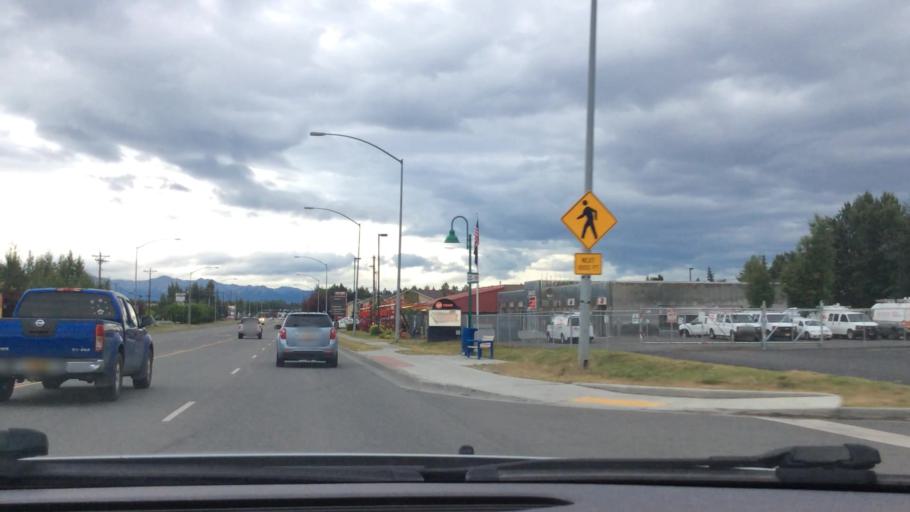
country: US
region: Alaska
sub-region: Anchorage Municipality
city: Anchorage
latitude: 61.1719
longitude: -149.8383
